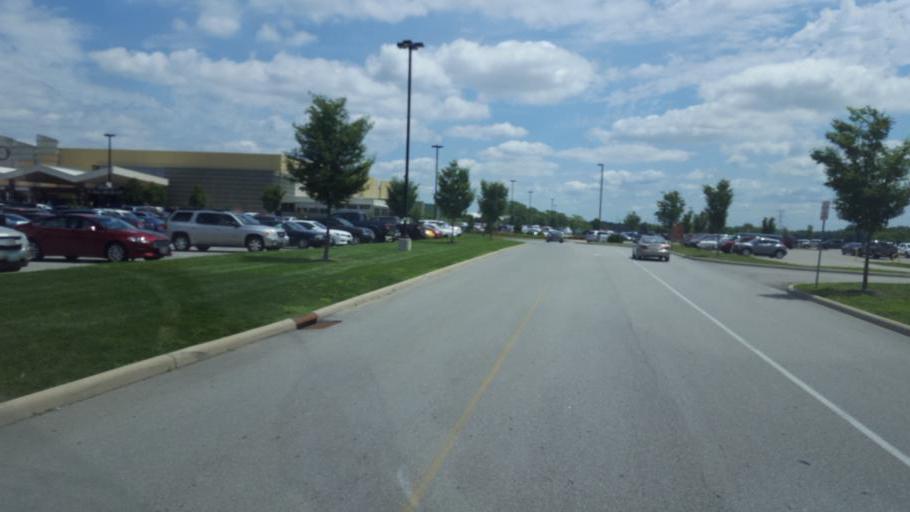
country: US
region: Ohio
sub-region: Franklin County
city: Obetz
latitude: 39.8382
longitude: -82.9992
